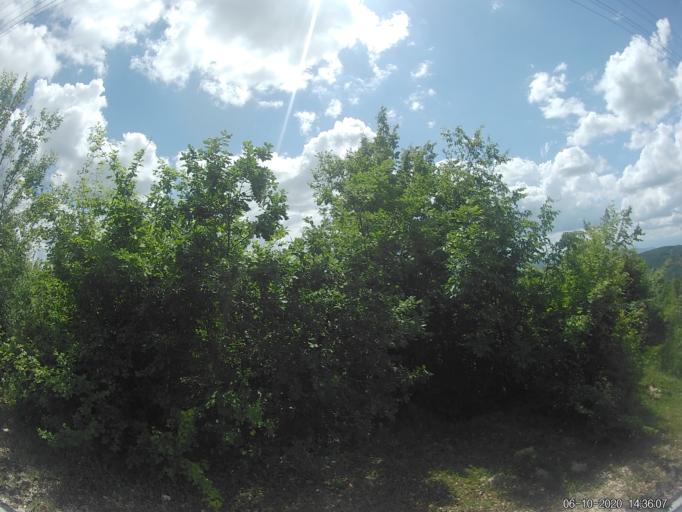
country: XK
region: Prizren
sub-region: Komuna e Therandes
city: Budakovo
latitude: 42.4116
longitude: 20.9362
